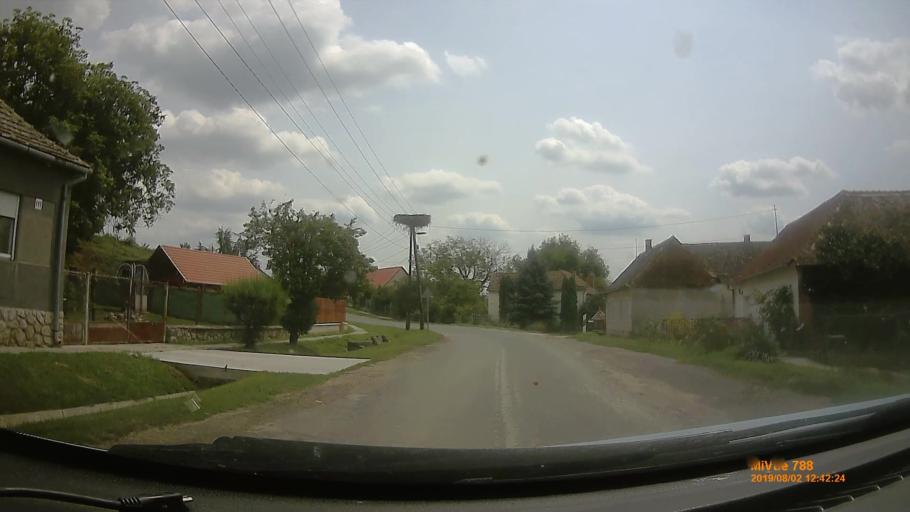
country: HU
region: Baranya
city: Buekkoesd
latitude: 46.0895
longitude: 17.9763
